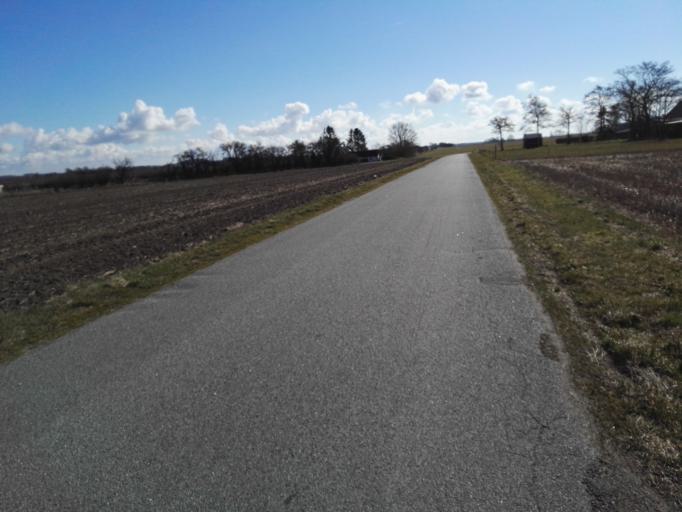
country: DK
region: Zealand
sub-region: Lejre Kommune
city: Ejby
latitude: 55.7756
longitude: 11.8188
